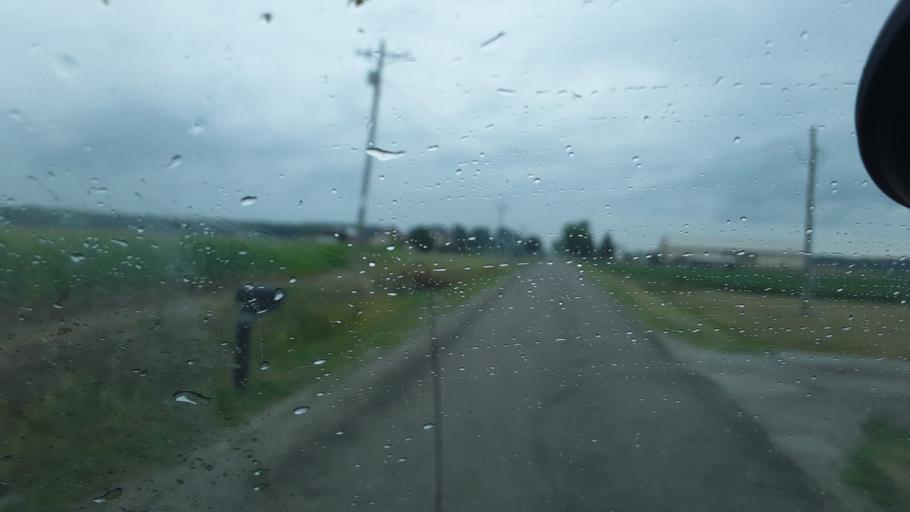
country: US
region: Ohio
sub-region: Defiance County
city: Hicksville
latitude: 41.3033
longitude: -84.6700
